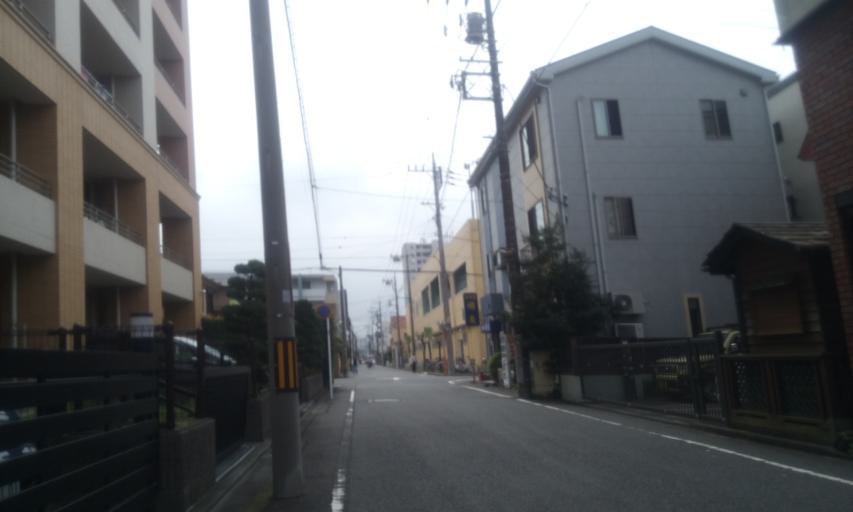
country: JP
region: Tokyo
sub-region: Machida-shi
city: Machida
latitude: 35.5742
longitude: 139.3834
